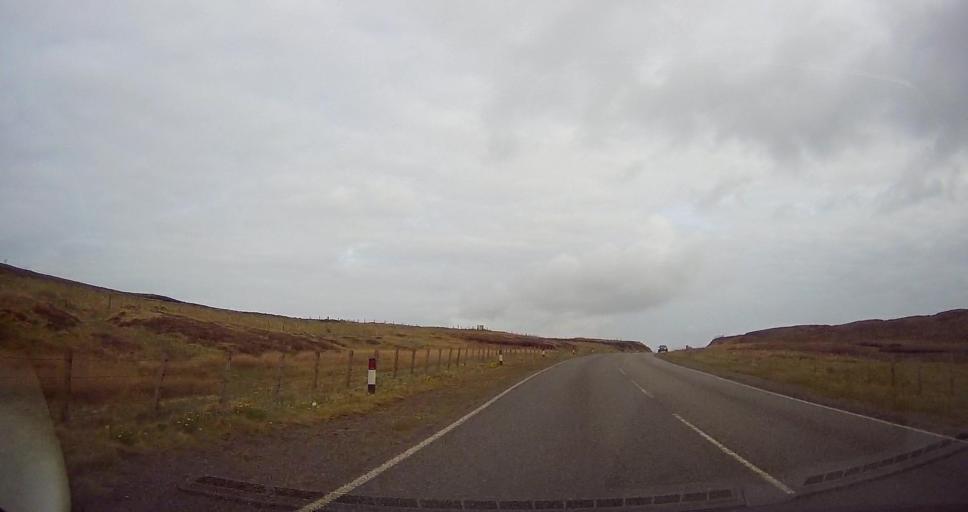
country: GB
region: Scotland
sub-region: Shetland Islands
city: Sandwick
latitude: 60.0859
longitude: -1.2320
